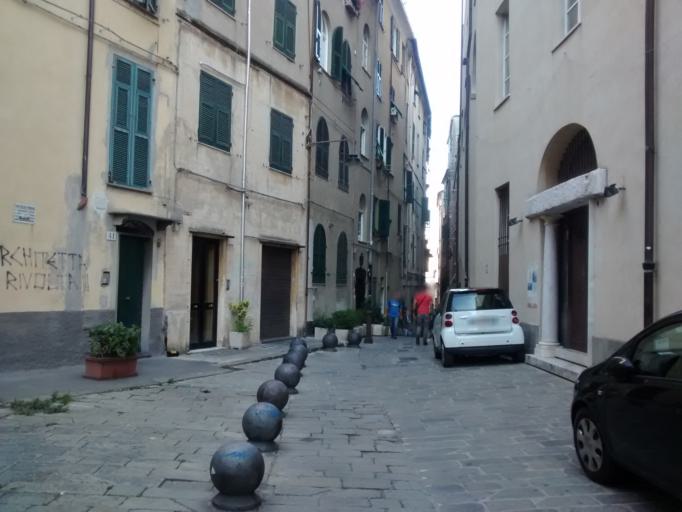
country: IT
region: Liguria
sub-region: Provincia di Genova
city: San Teodoro
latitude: 44.4043
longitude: 8.9301
